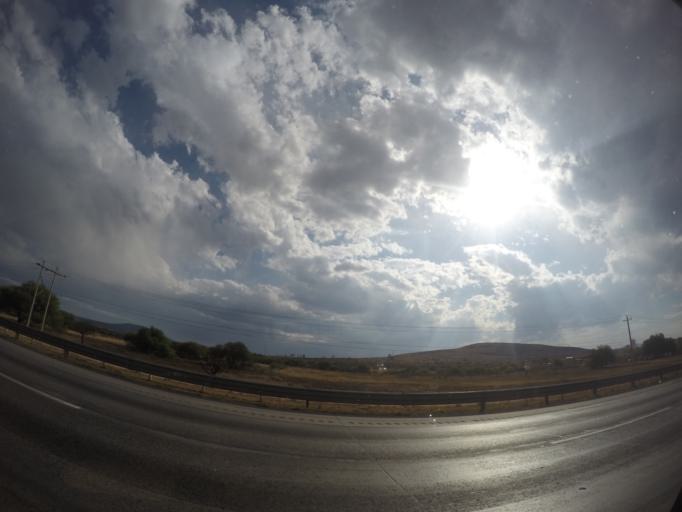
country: MX
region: Hidalgo
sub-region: Tepeji del Rio de Ocampo
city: Santiago Tlautla
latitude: 19.9854
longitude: -99.4426
